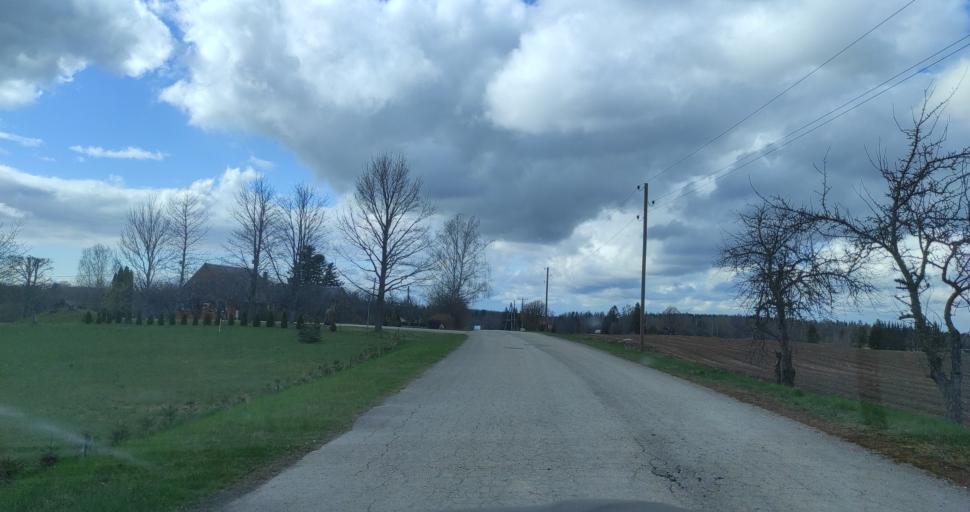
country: LV
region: Aizpute
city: Aizpute
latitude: 56.7128
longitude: 21.5764
